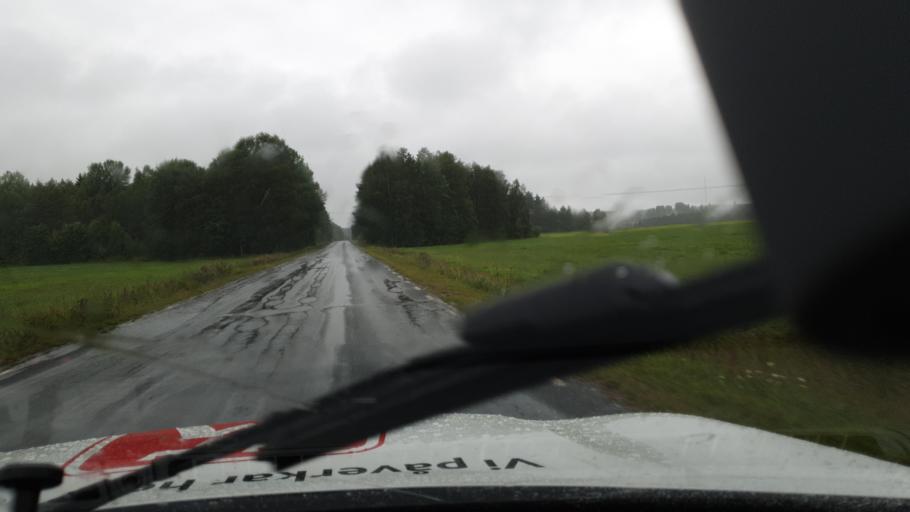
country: SE
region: Vaesterbotten
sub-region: Skelleftea Kommun
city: Viken
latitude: 64.5839
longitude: 20.9714
